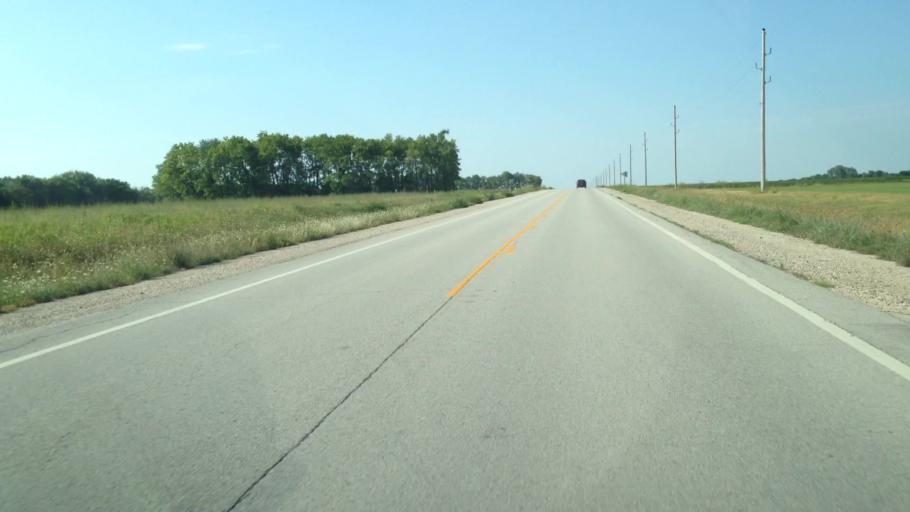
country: US
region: Kansas
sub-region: Anderson County
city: Garnett
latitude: 38.0416
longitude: -95.1697
